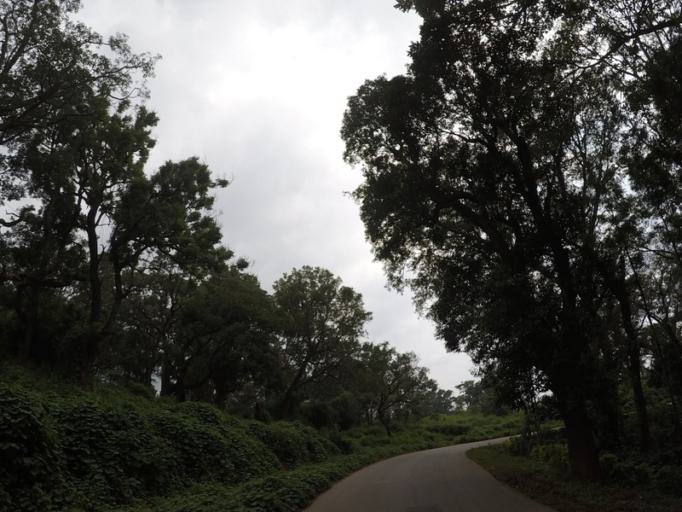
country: IN
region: Karnataka
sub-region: Chikmagalur
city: Chikmagalur
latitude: 13.4569
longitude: 75.7992
